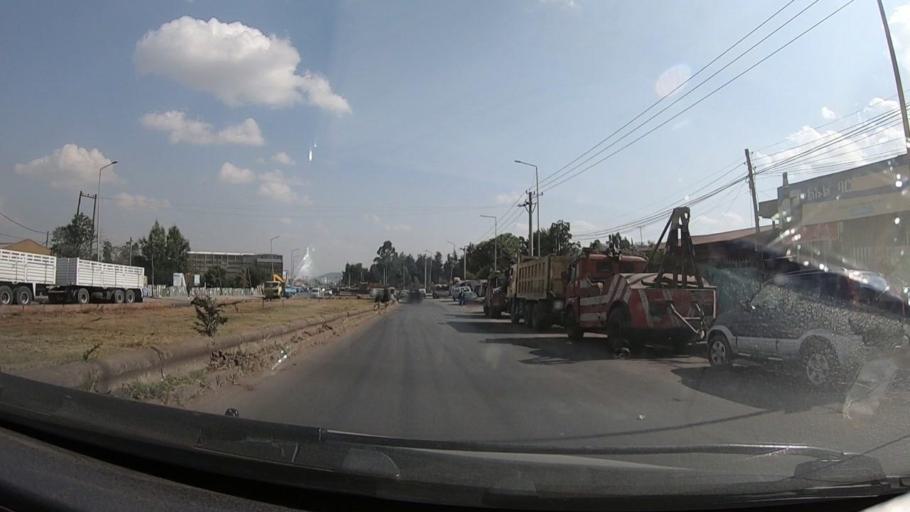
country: ET
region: Adis Abeba
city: Addis Ababa
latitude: 8.9861
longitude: 38.6941
